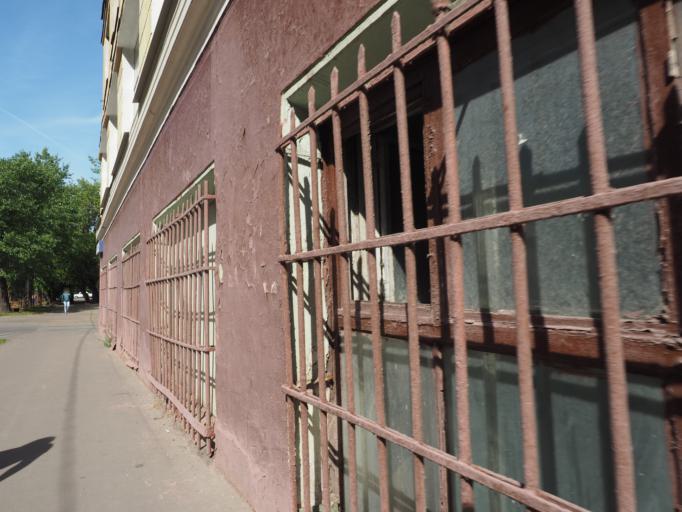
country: RU
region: Moscow
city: Lefortovo
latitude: 55.7781
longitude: 37.7336
